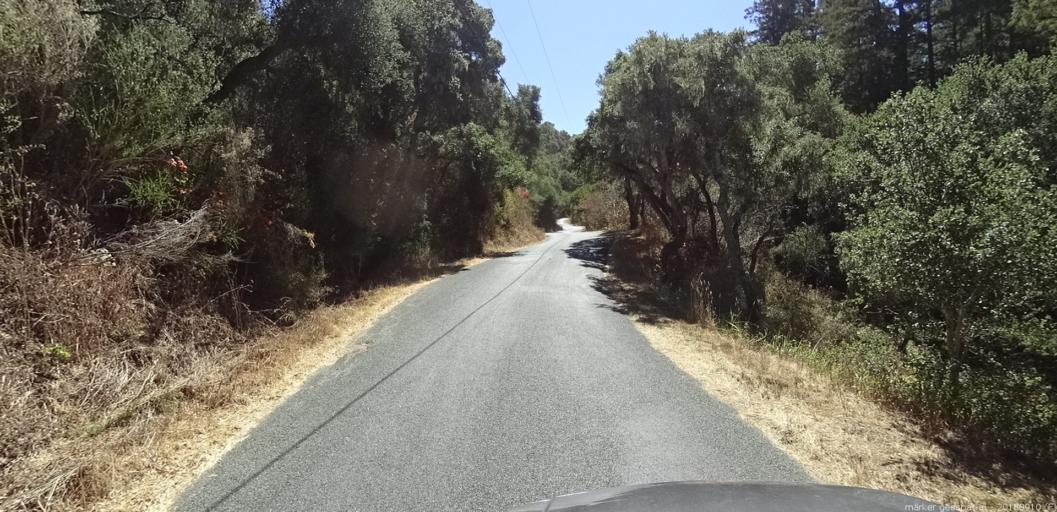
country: US
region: California
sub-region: Monterey County
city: Carmel Valley Village
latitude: 36.5087
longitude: -121.8093
